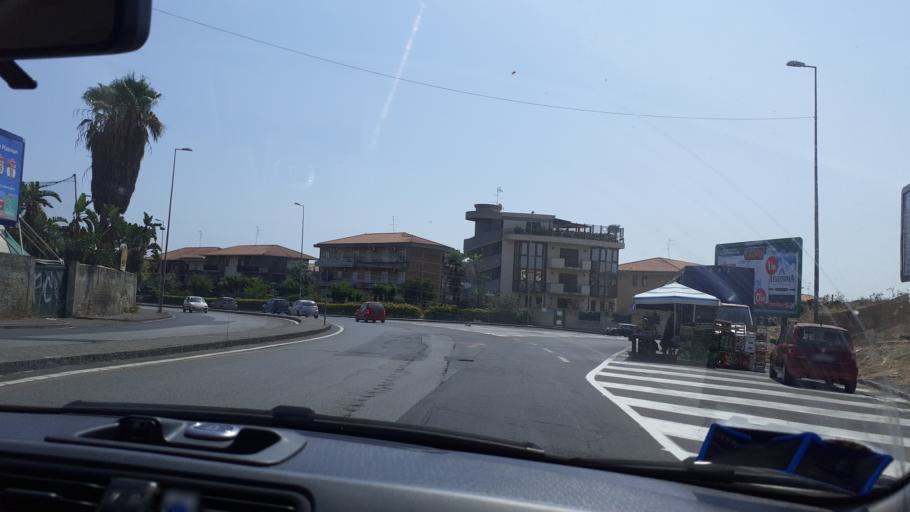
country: IT
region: Sicily
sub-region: Catania
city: Misterbianco
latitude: 37.5136
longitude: 15.0542
